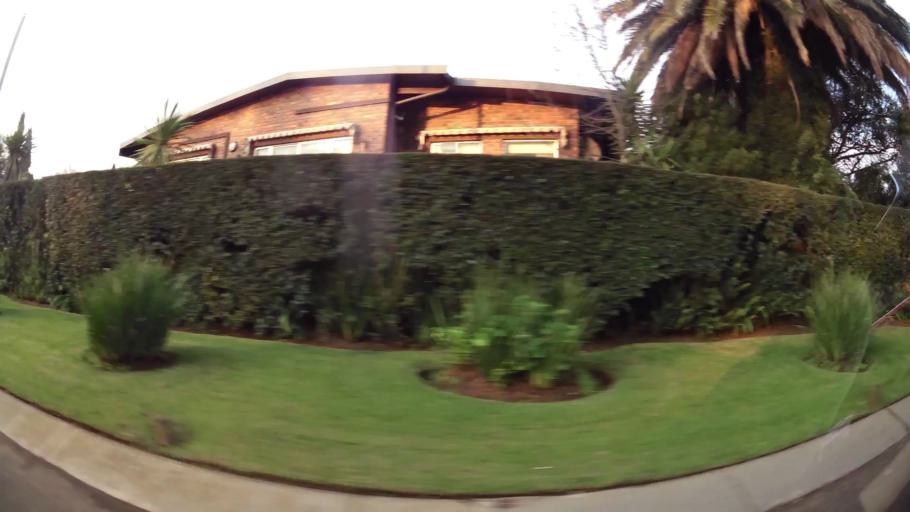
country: ZA
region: Gauteng
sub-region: Ekurhuleni Metropolitan Municipality
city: Benoni
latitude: -26.1662
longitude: 28.2888
